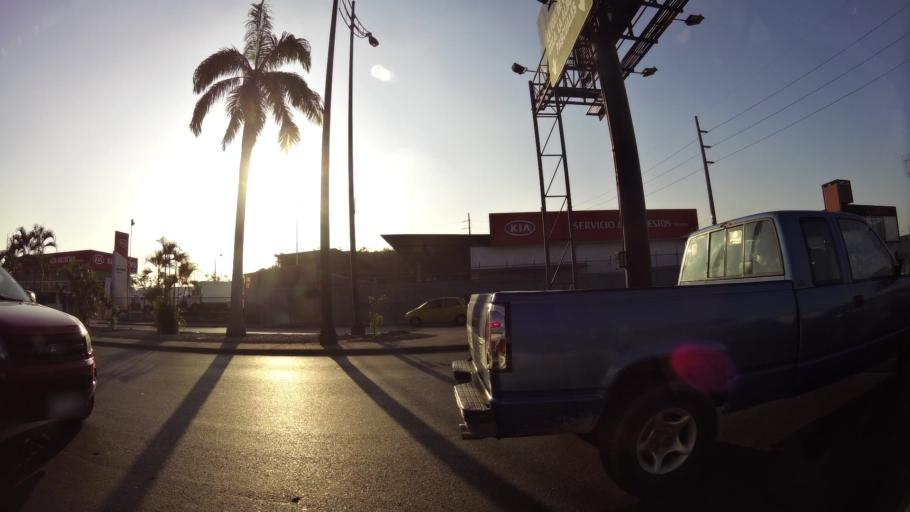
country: EC
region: Guayas
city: Eloy Alfaro
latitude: -2.1570
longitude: -79.8971
